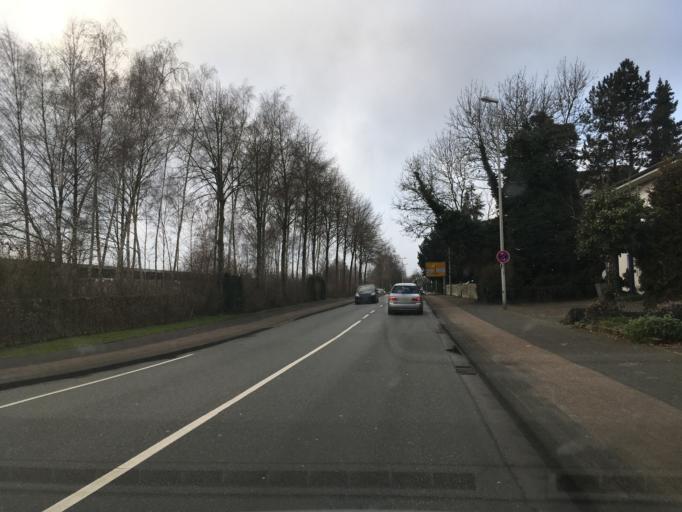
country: DE
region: North Rhine-Westphalia
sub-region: Regierungsbezirk Munster
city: Gronau
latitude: 52.2157
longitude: 7.0227
